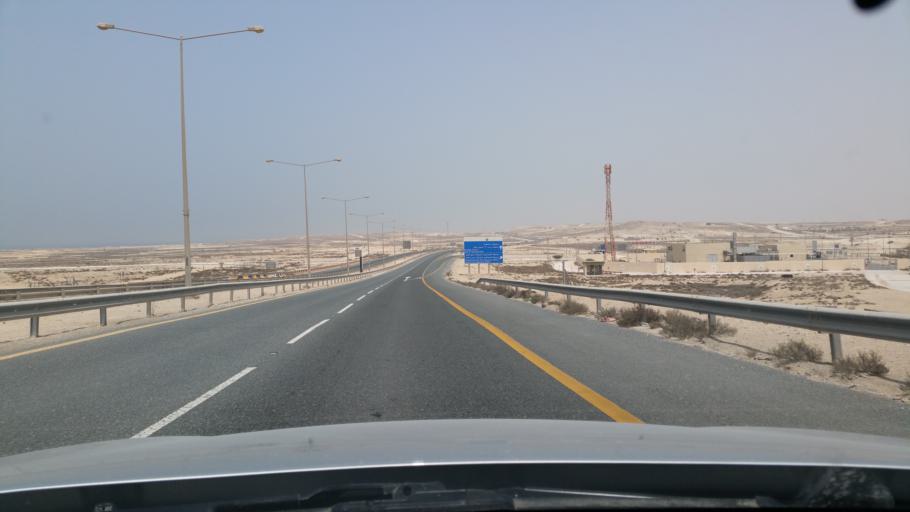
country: QA
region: Baladiyat ar Rayyan
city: Dukhan
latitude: 25.3318
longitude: 50.7848
